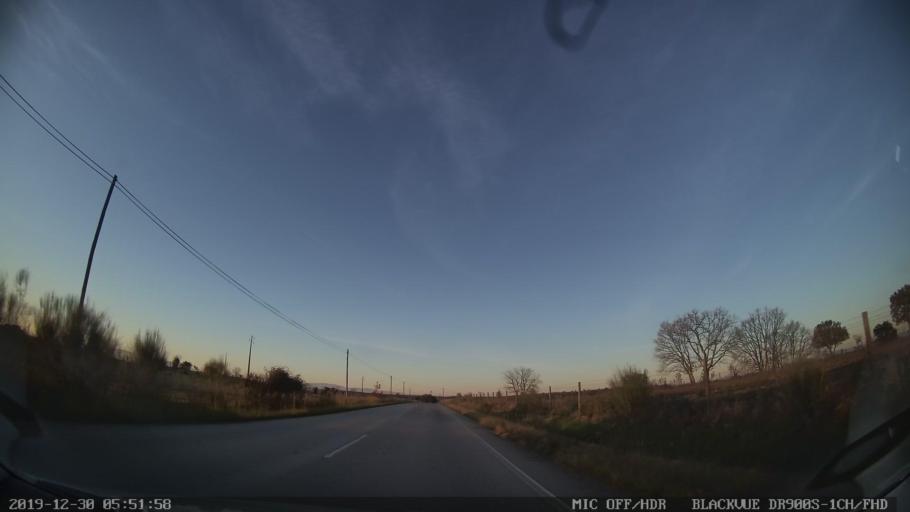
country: PT
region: Castelo Branco
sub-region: Idanha-A-Nova
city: Idanha-a-Nova
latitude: 40.0003
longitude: -7.2471
